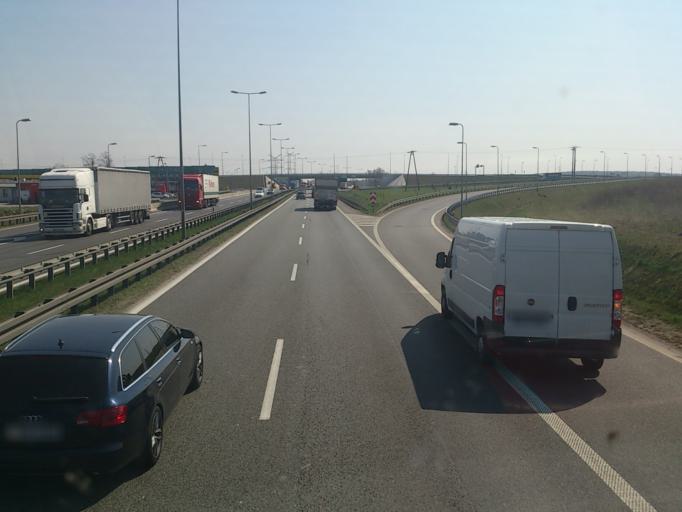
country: PL
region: Silesian Voivodeship
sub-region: Powiat bedzinski
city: Siewierz
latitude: 50.4633
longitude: 19.2309
